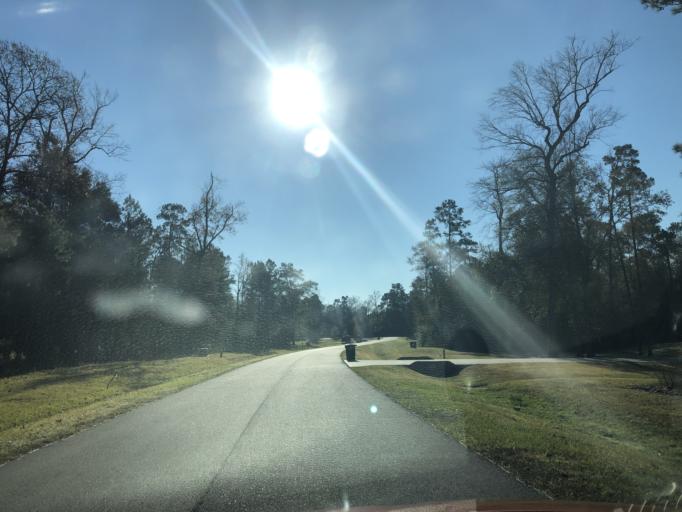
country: US
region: Texas
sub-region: Montgomery County
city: Porter Heights
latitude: 30.0671
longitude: -95.3235
